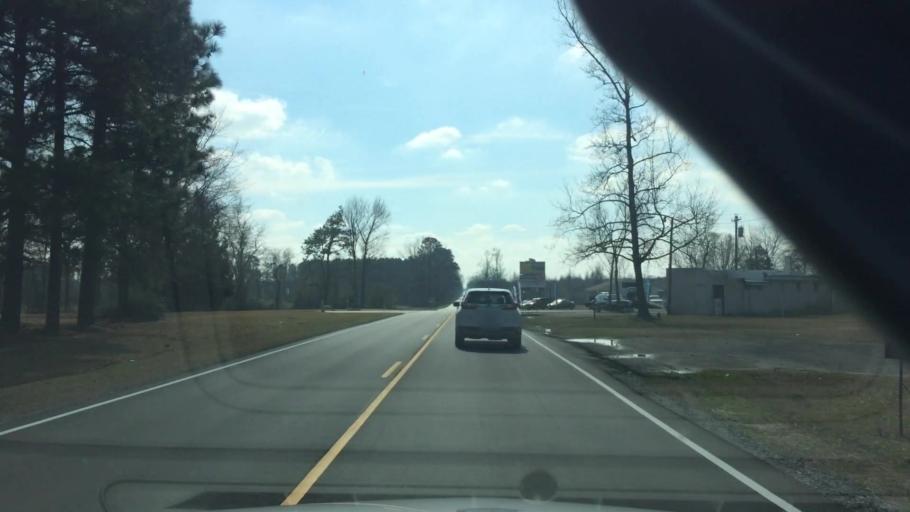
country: US
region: North Carolina
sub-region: Duplin County
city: Beulaville
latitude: 34.9554
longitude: -77.7659
